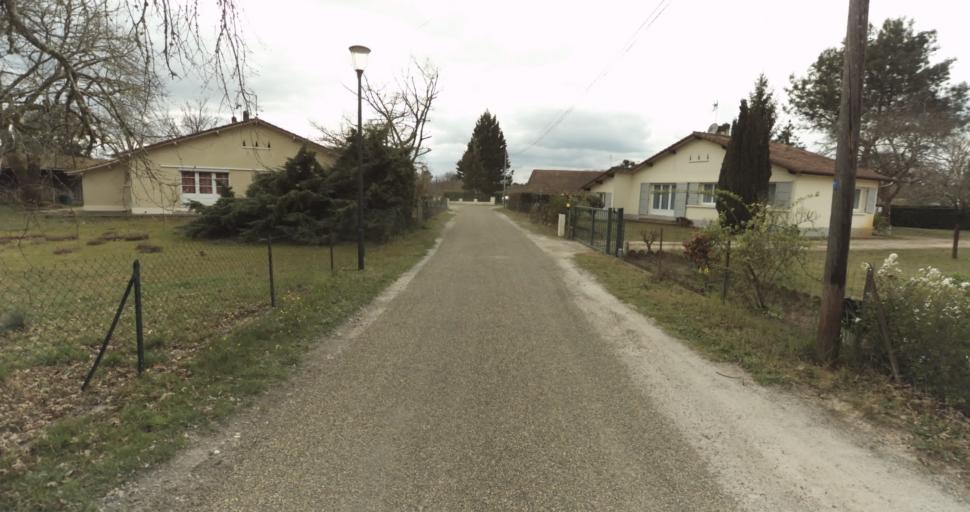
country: FR
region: Aquitaine
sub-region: Departement des Landes
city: Roquefort
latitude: 44.0479
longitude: -0.3242
